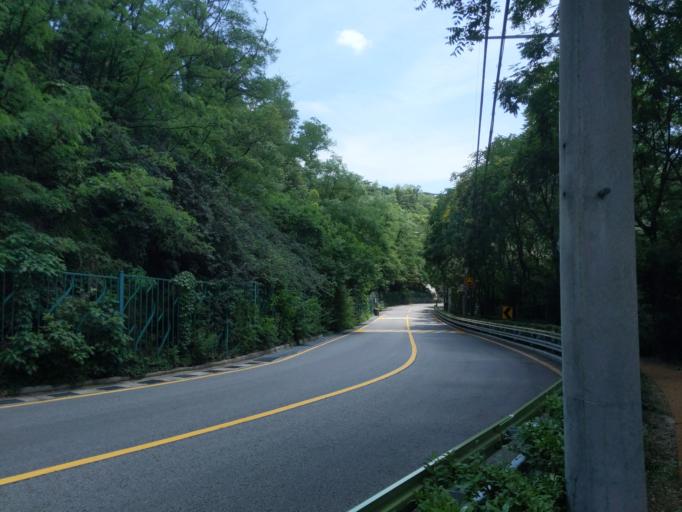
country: KR
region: Seoul
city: Seoul
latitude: 37.5987
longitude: 126.9734
